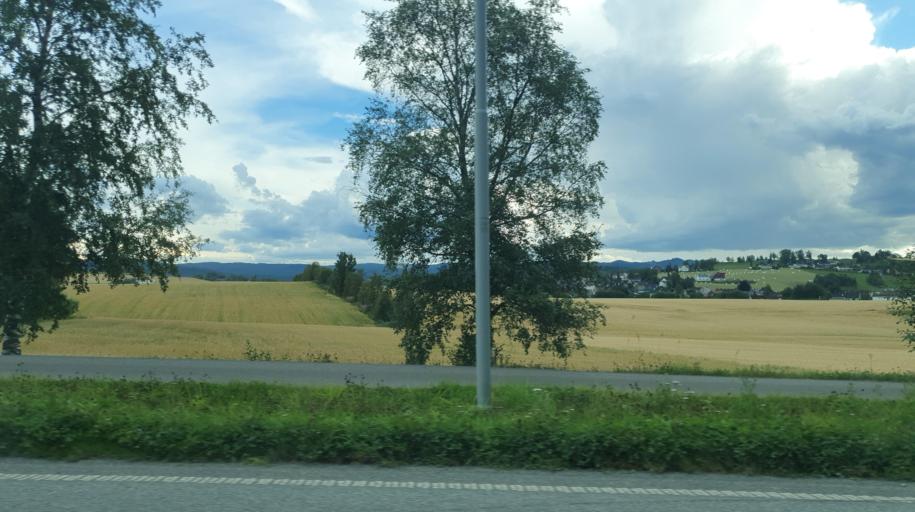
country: NO
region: Nord-Trondelag
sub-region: Levanger
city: Levanger
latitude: 63.7511
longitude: 11.3286
